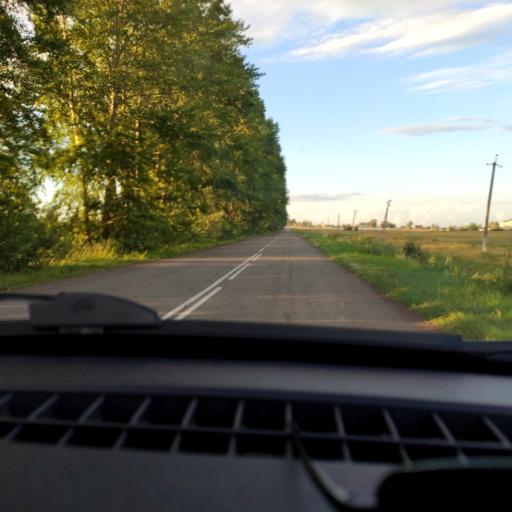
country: RU
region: Bashkortostan
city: Avdon
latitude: 54.4923
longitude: 55.6071
